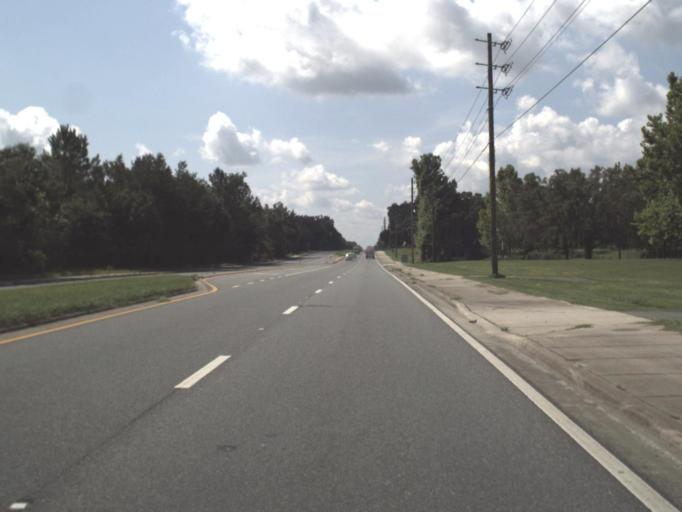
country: US
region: Florida
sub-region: Citrus County
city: Inverness Highlands South
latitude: 28.8064
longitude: -82.3124
